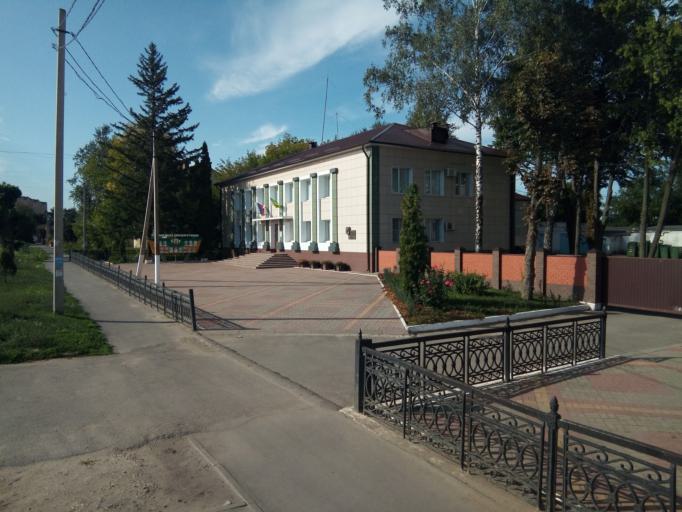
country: RU
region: Lipetsk
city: Lipetsk
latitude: 52.6303
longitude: 39.5529
